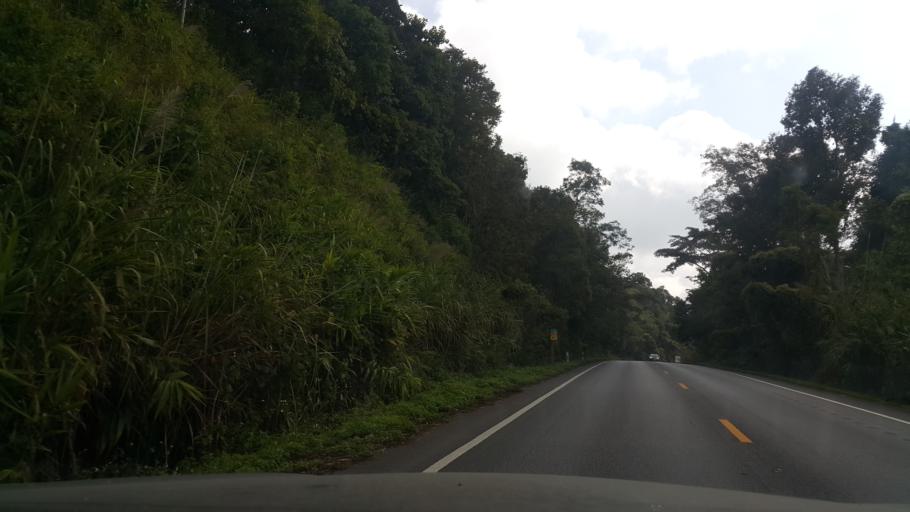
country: TH
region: Phayao
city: Phayao
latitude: 19.0665
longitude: 99.7720
